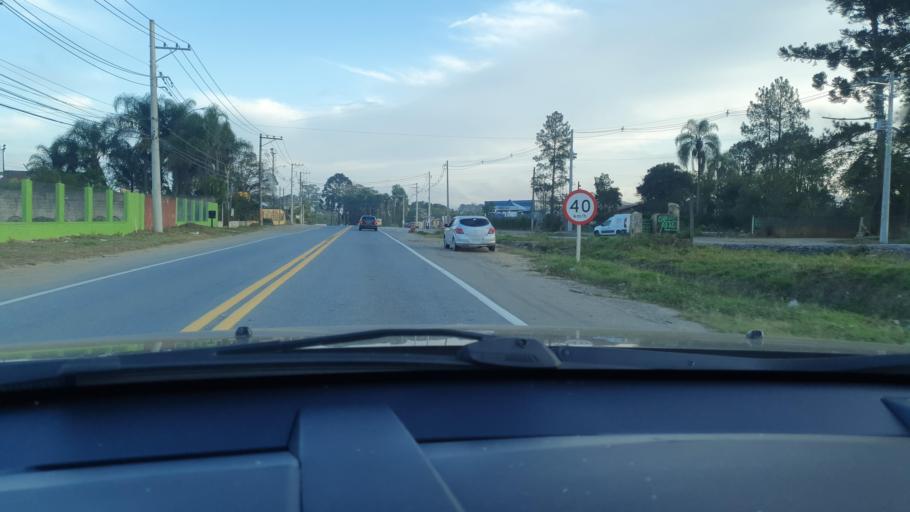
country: BR
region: Sao Paulo
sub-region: Ibiuna
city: Ibiuna
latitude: -23.6522
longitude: -47.1272
